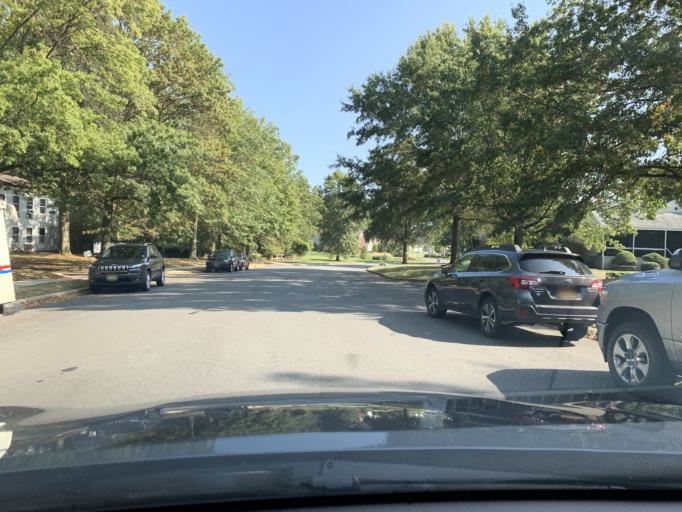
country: US
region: New Jersey
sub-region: Monmouth County
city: Shrewsbury
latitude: 40.3171
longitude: -74.0592
